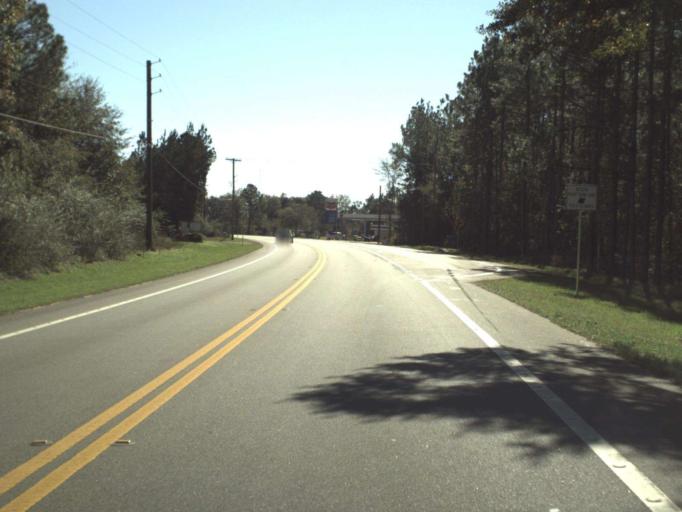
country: US
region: Florida
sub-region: Okaloosa County
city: Crestview
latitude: 30.7863
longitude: -86.6836
